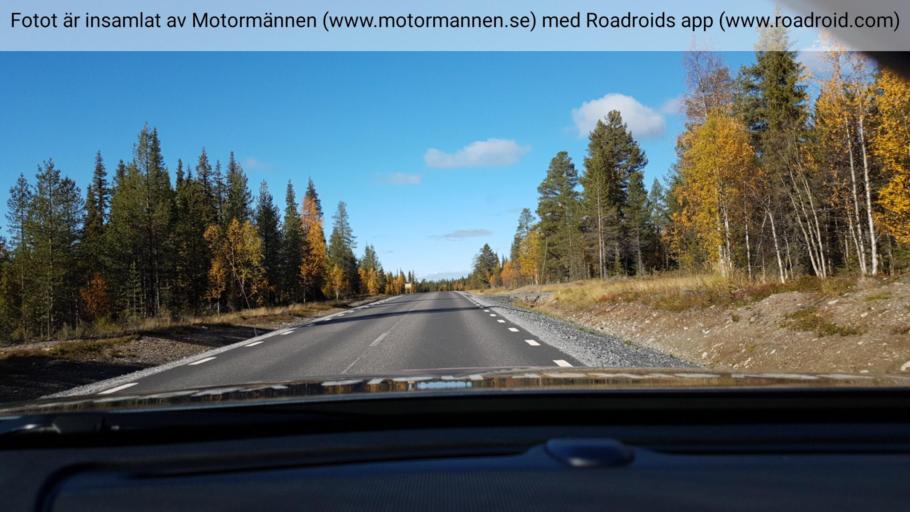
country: SE
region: Norrbotten
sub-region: Gallivare Kommun
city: Gaellivare
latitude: 66.9424
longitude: 20.8119
